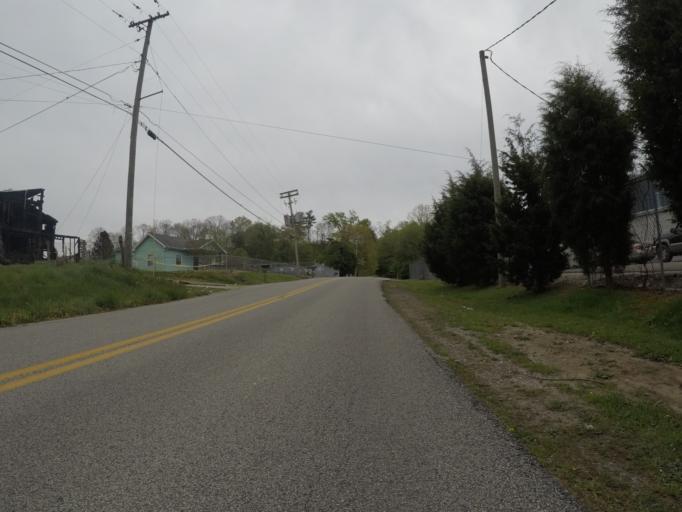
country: US
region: West Virginia
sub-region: Cabell County
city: Pea Ridge
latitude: 38.4144
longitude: -82.3400
